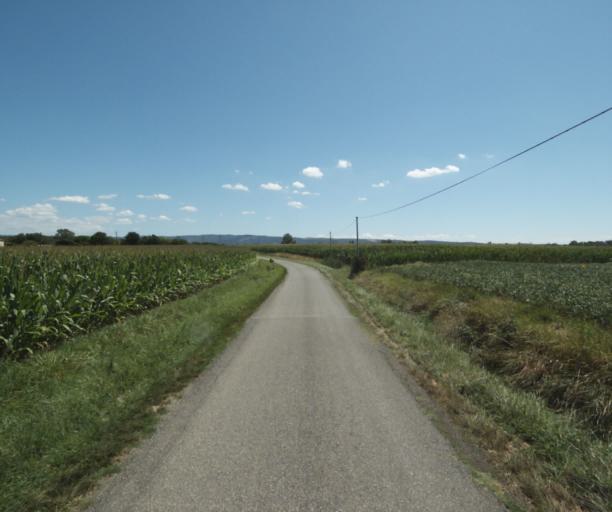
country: FR
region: Midi-Pyrenees
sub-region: Departement de la Haute-Garonne
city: Saint-Felix-Lauragais
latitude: 43.4558
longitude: 1.9312
